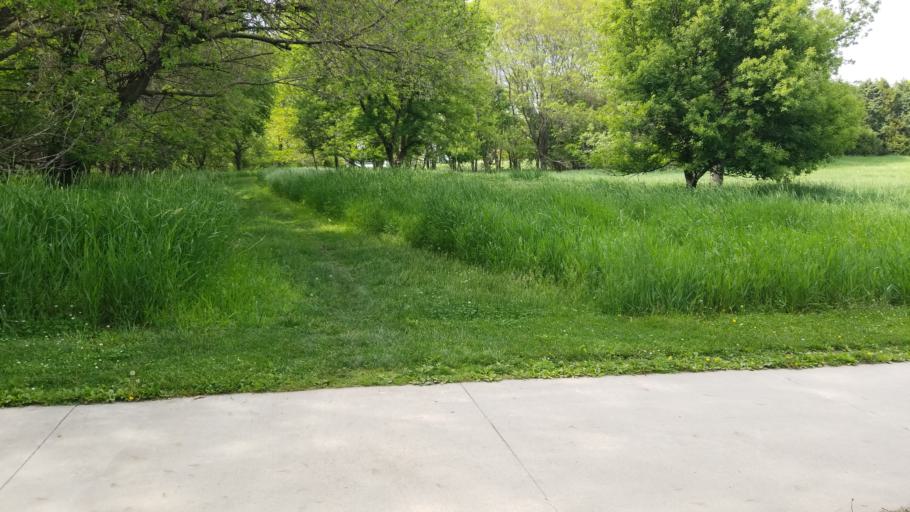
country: US
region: Nebraska
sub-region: Sarpy County
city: Chalco
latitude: 41.1716
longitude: -96.1655
